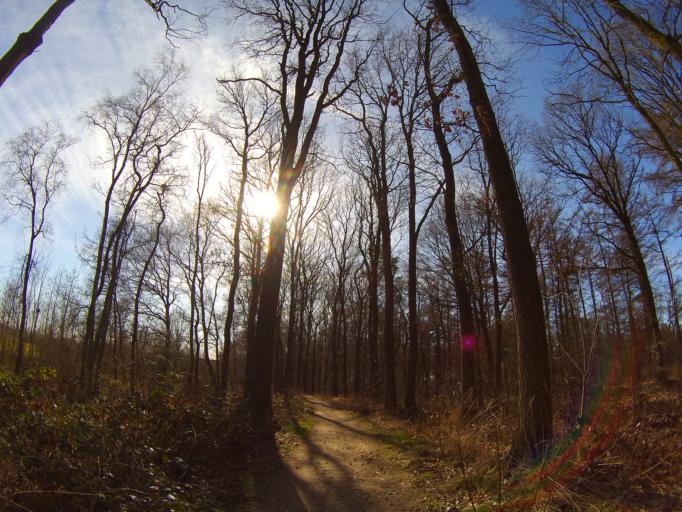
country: NL
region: Utrecht
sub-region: Gemeente Utrechtse Heuvelrug
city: Overberg
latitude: 52.0802
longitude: 5.5262
